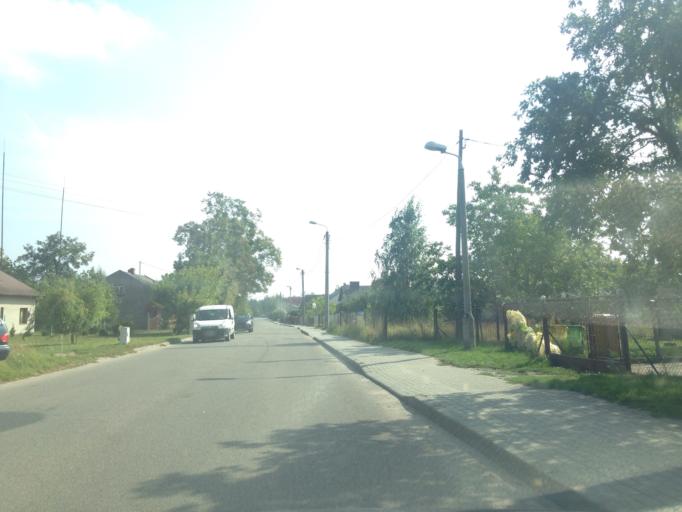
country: PL
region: Kujawsko-Pomorskie
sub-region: Powiat brodnicki
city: Brodnica
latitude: 53.2737
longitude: 19.4133
